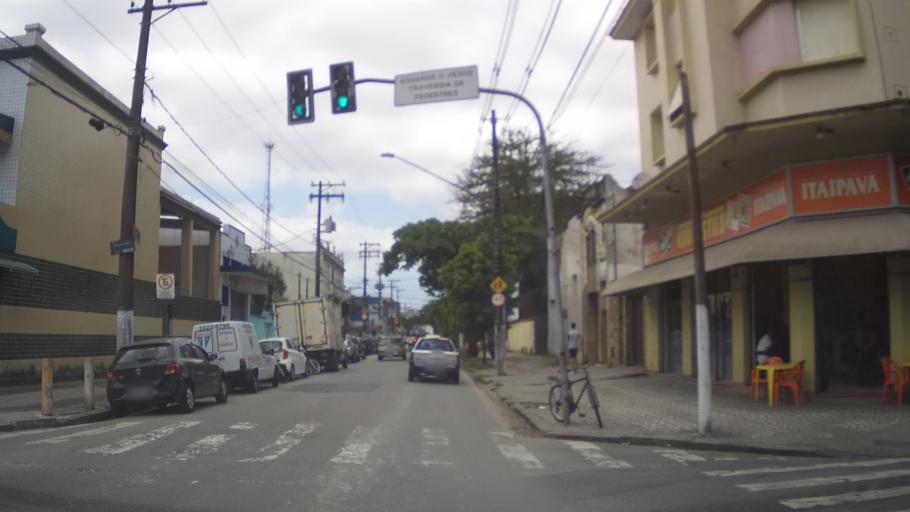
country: BR
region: Sao Paulo
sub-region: Santos
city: Santos
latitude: -23.9519
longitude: -46.3209
